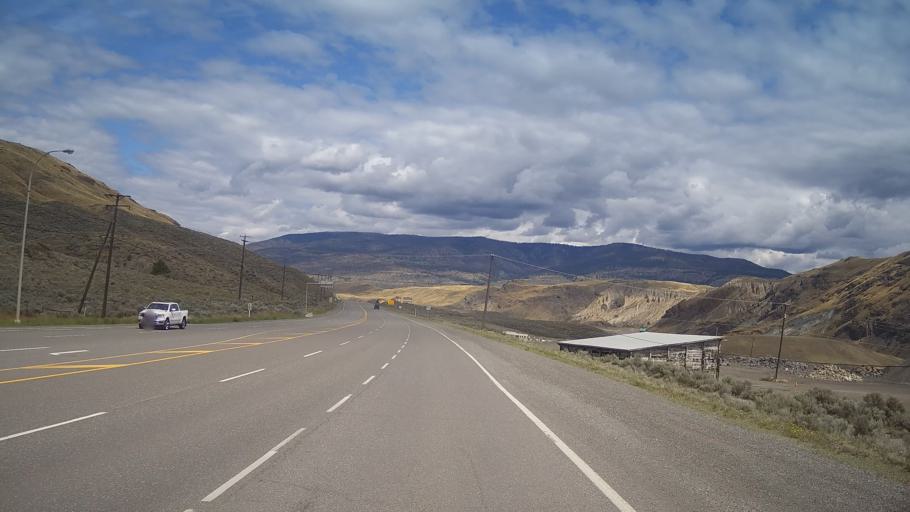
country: CA
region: British Columbia
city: Cache Creek
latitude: 50.7738
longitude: -121.3129
